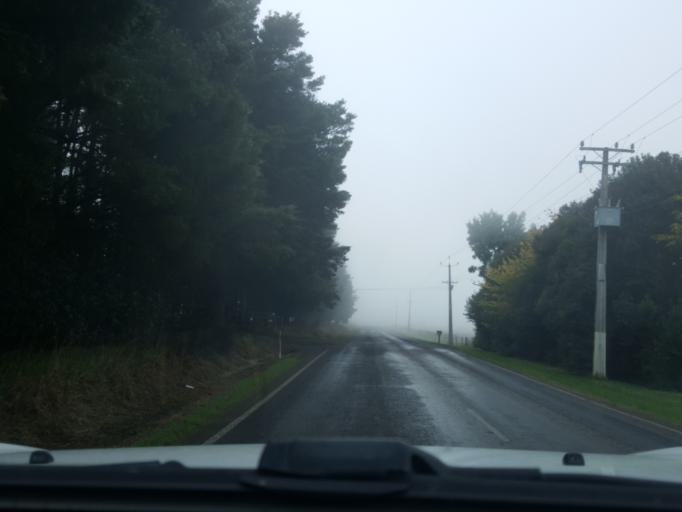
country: NZ
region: Auckland
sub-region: Auckland
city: Pukekohe East
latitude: -37.3011
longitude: 175.0237
